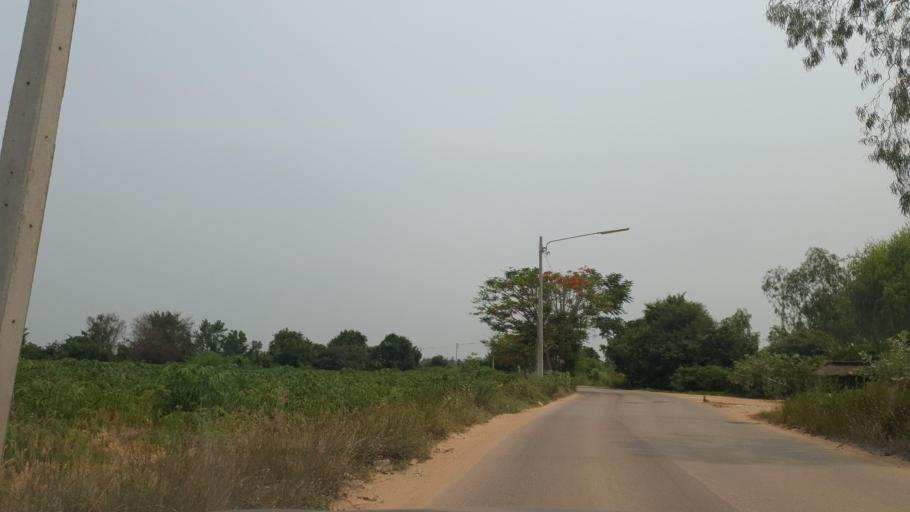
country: TH
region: Chon Buri
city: Phatthaya
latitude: 12.8869
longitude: 100.9266
